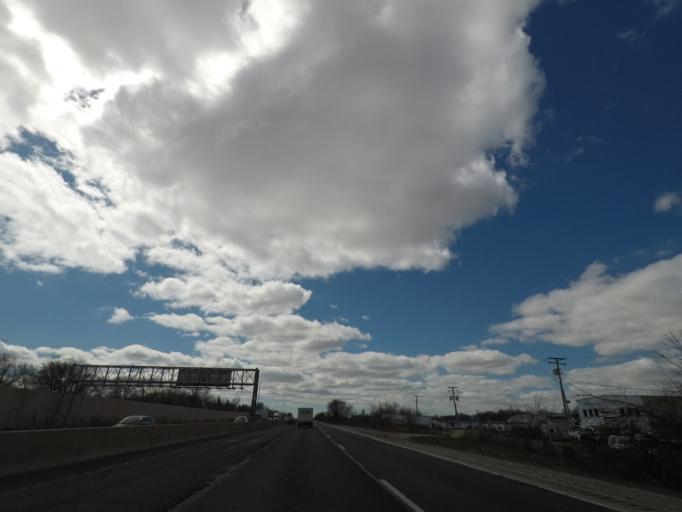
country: US
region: Illinois
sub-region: Will County
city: Crystal Lawns
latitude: 41.5549
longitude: -88.1806
